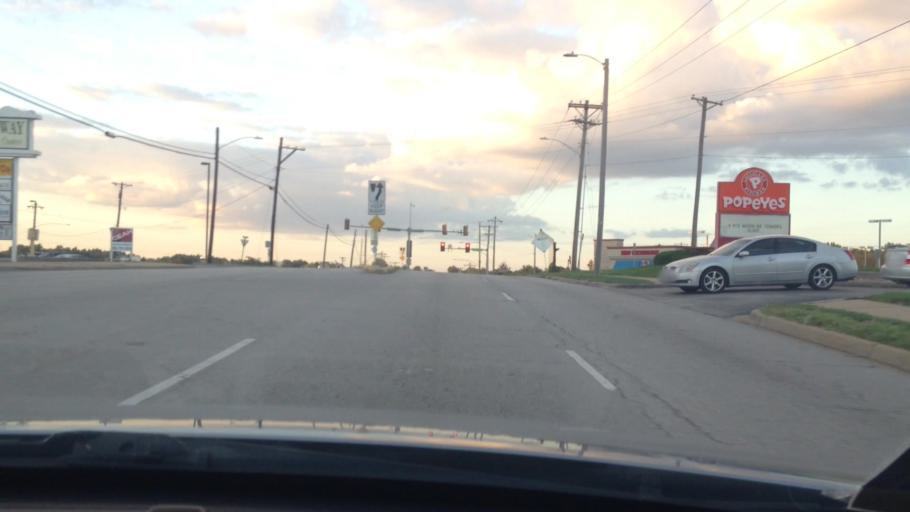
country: US
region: Missouri
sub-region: Jackson County
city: Raytown
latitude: 38.9853
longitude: -94.4645
